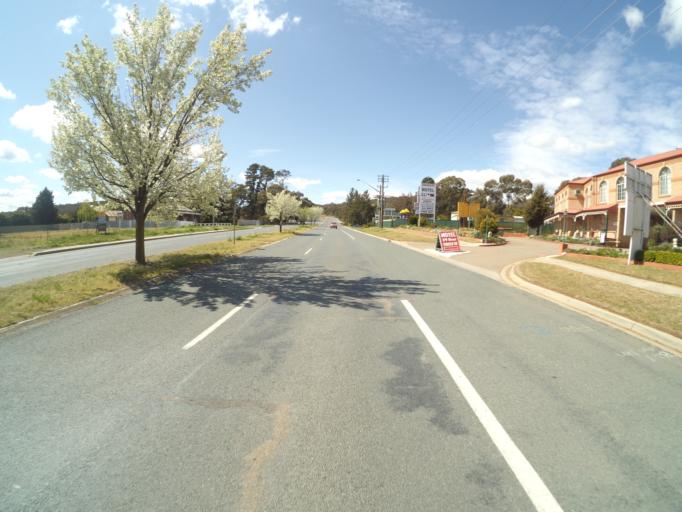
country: AU
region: New South Wales
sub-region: Goulburn Mulwaree
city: Goulburn
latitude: -34.7474
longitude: 149.7511
